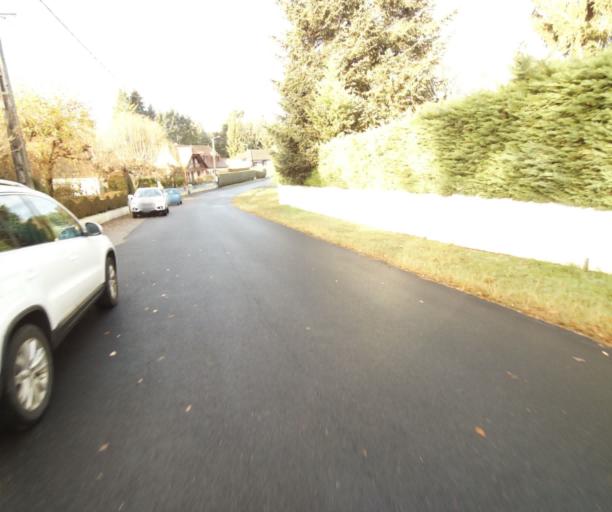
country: FR
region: Limousin
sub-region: Departement de la Correze
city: Saint-Mexant
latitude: 45.2661
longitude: 1.6316
